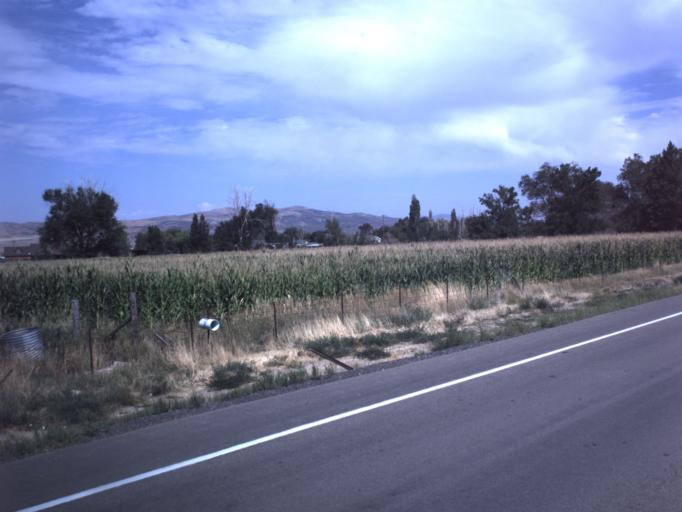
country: US
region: Utah
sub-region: Juab County
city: Nephi
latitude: 39.5488
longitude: -111.8638
